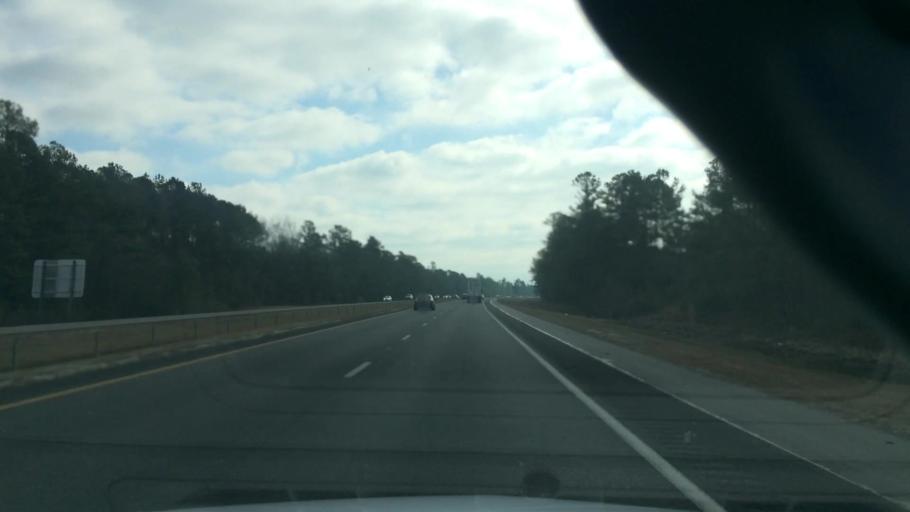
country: US
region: North Carolina
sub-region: Pender County
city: Burgaw
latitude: 34.5643
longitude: -77.8972
